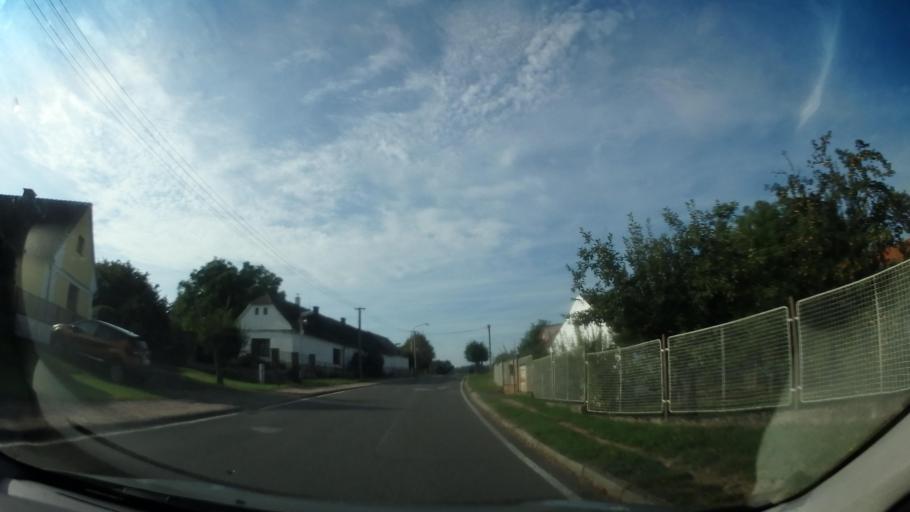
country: CZ
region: Jihocesky
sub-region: Okres Pisek
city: Pisek
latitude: 49.3890
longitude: 14.1277
